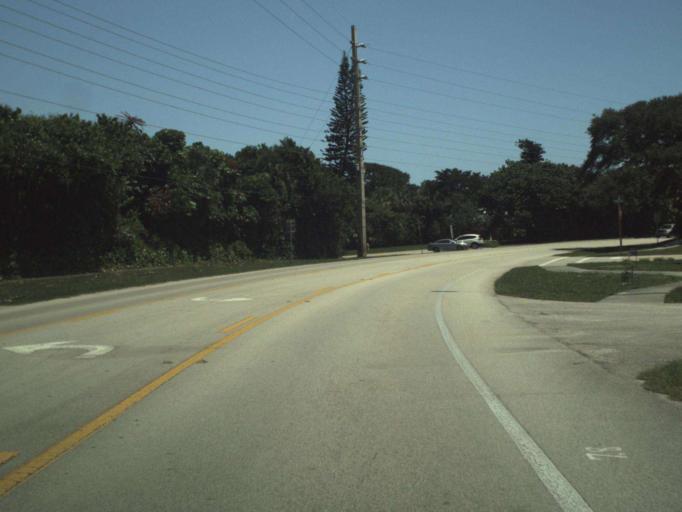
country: US
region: Florida
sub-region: Indian River County
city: Vero Beach
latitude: 27.6628
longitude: -80.3617
